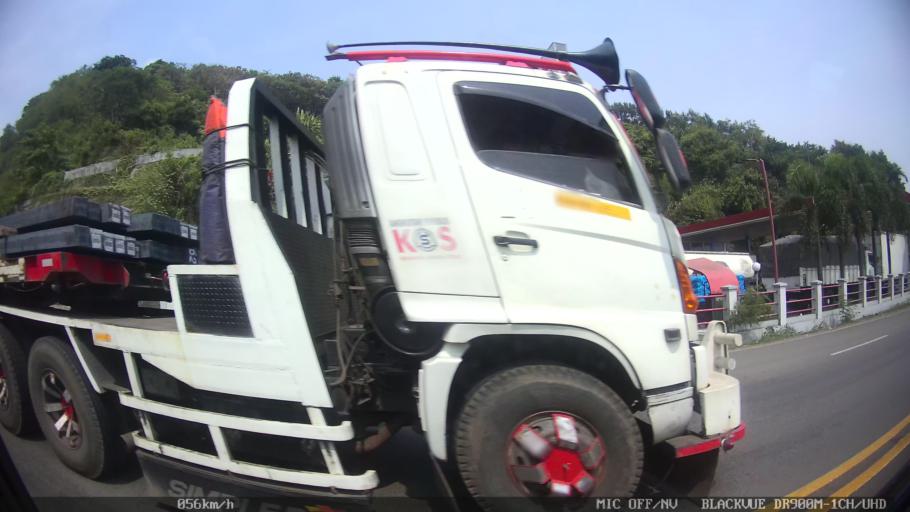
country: ID
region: Banten
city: Curug
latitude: -5.9501
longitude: 106.0021
